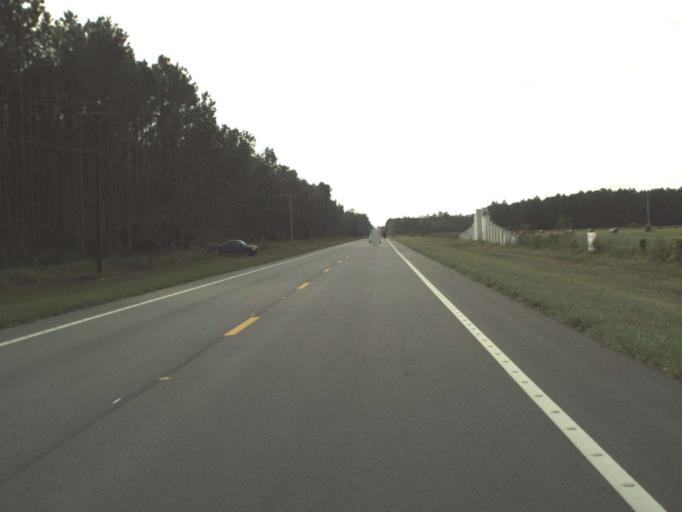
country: US
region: Florida
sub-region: Gulf County
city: Wewahitchka
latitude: 30.1347
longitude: -85.3626
